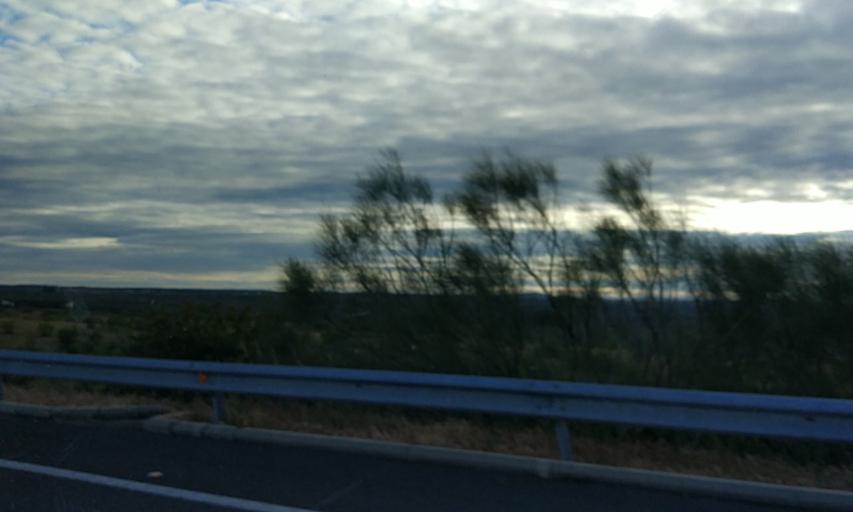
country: ES
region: Extremadura
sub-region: Provincia de Caceres
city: Hinojal
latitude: 39.6882
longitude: -6.3985
